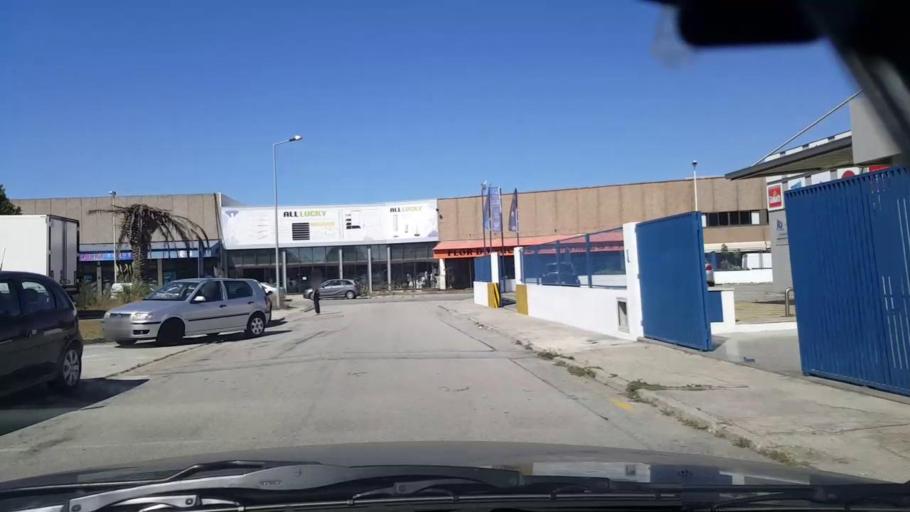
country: PT
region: Porto
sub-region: Vila do Conde
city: Arvore
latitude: 41.3289
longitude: -8.7151
